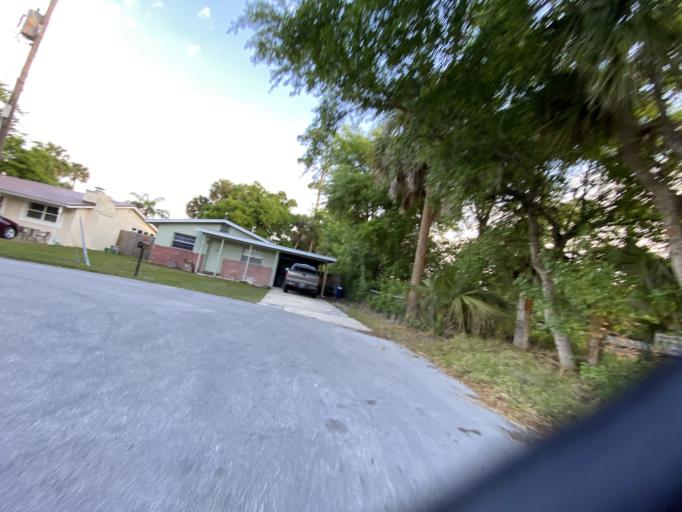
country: US
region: Florida
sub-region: Volusia County
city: South Daytona
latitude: 29.1747
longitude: -81.0079
